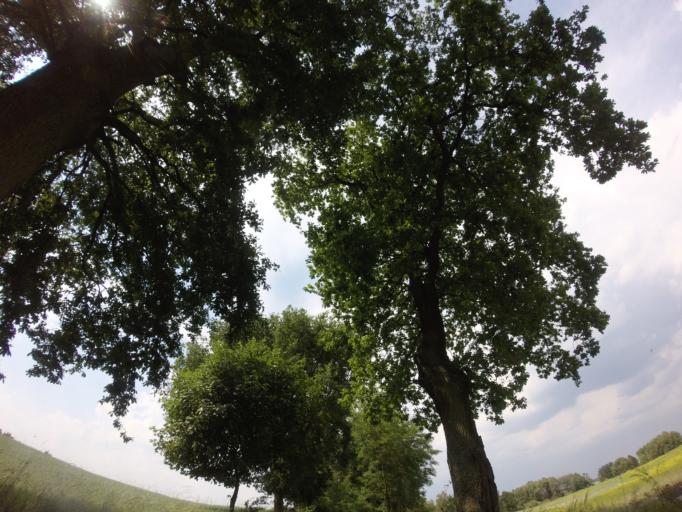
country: PL
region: West Pomeranian Voivodeship
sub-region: Powiat choszczenski
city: Krzecin
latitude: 53.1275
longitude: 15.5910
